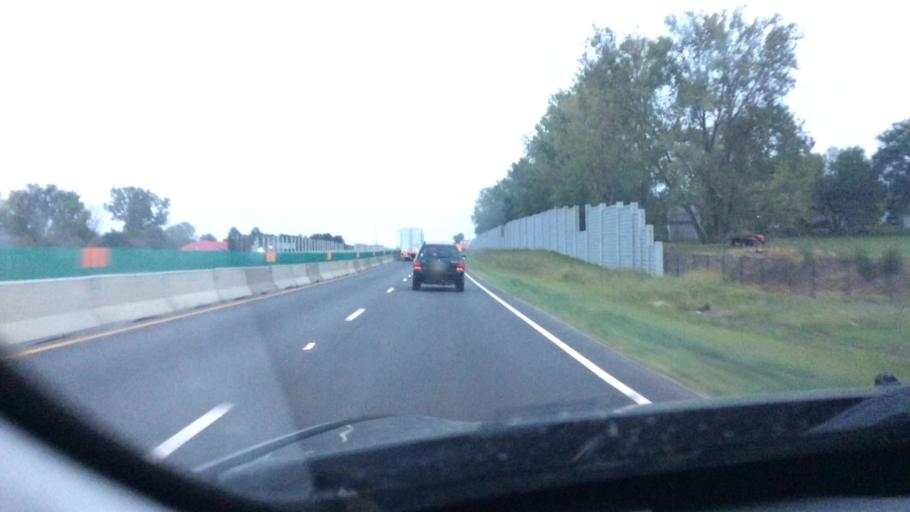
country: US
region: Ohio
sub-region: Hancock County
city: Findlay
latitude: 41.0724
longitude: -83.6620
